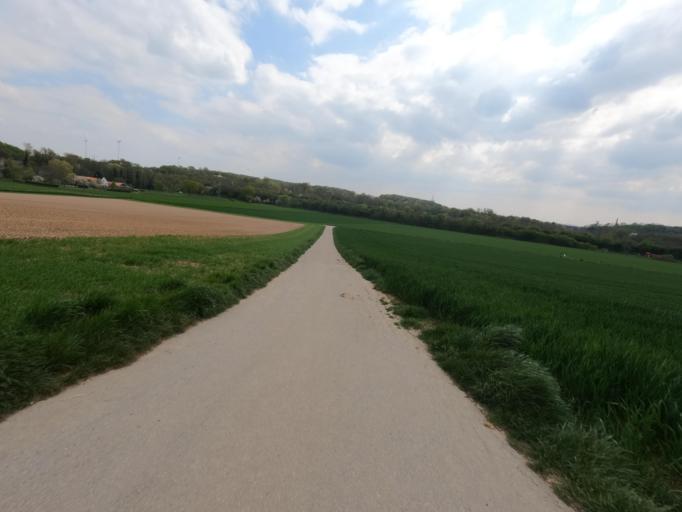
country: DE
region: North Rhine-Westphalia
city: Huckelhoven
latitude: 51.0726
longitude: 6.2196
